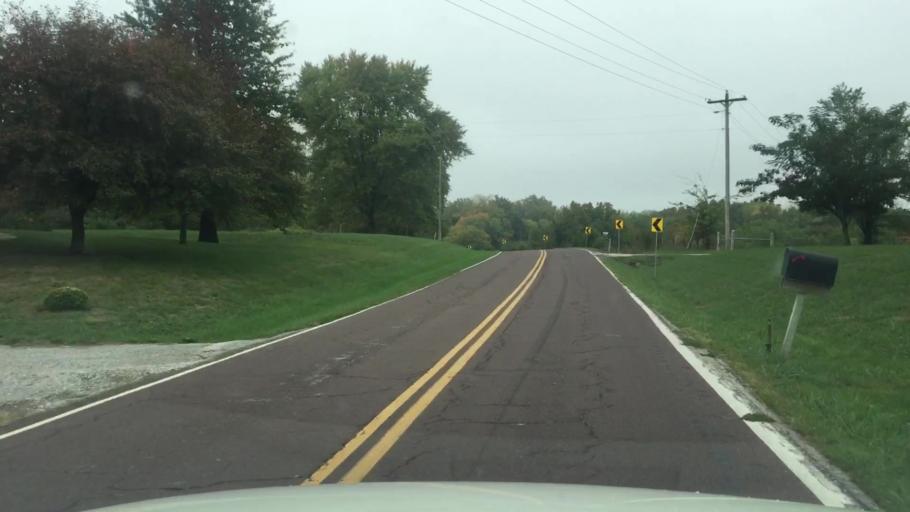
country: US
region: Missouri
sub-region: Boone County
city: Ashland
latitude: 38.8277
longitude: -92.3515
